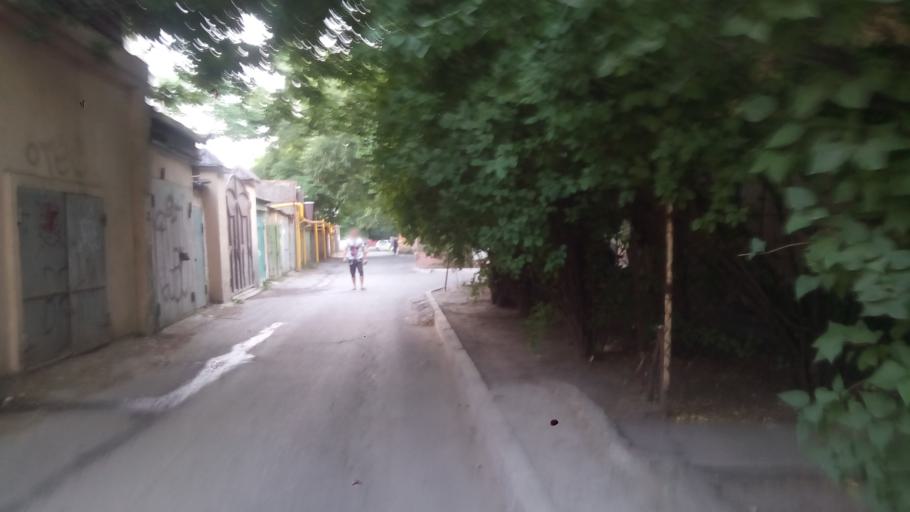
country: RU
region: Rostov
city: Rostov-na-Donu
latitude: 47.2491
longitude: 39.7502
